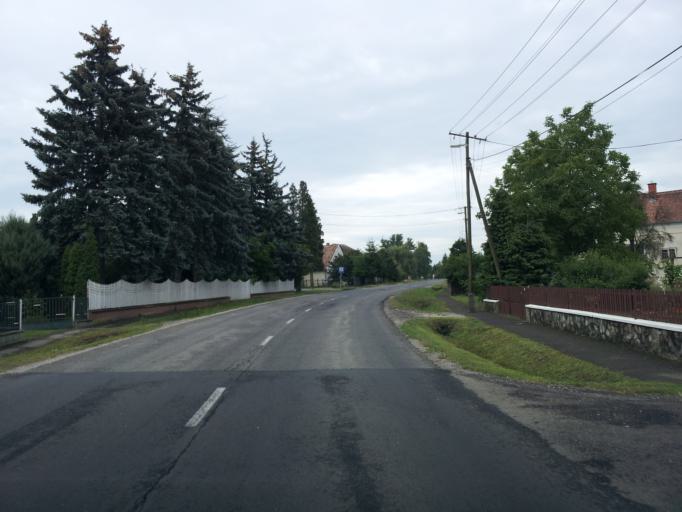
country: HU
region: Vas
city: Kormend
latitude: 46.9582
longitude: 16.6430
